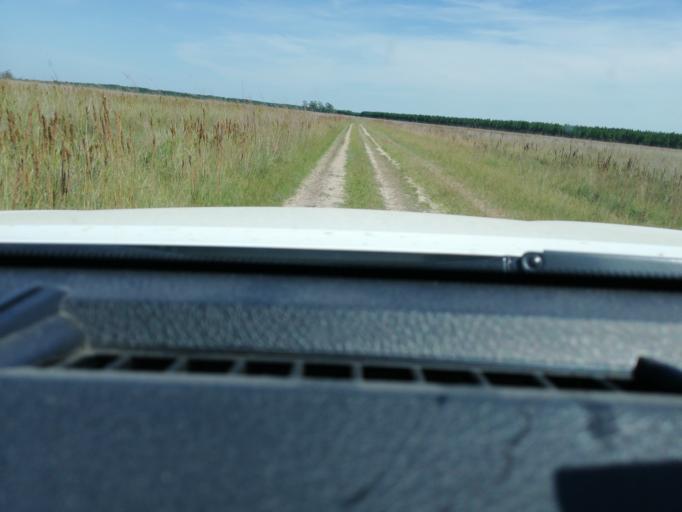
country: AR
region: Corrientes
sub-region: Departamento de San Miguel
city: San Miguel
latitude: -28.0444
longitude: -57.4573
